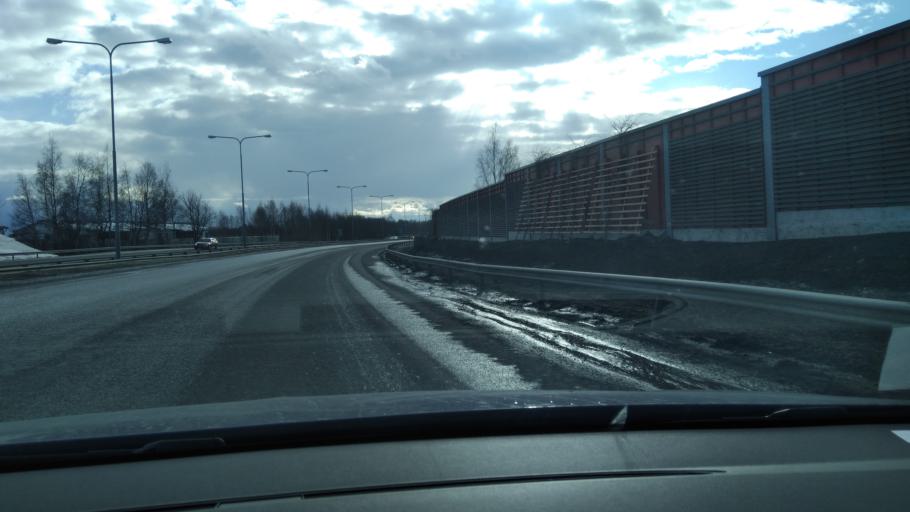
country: FI
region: Pirkanmaa
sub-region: Tampere
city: Pirkkala
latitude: 61.5064
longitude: 23.6859
